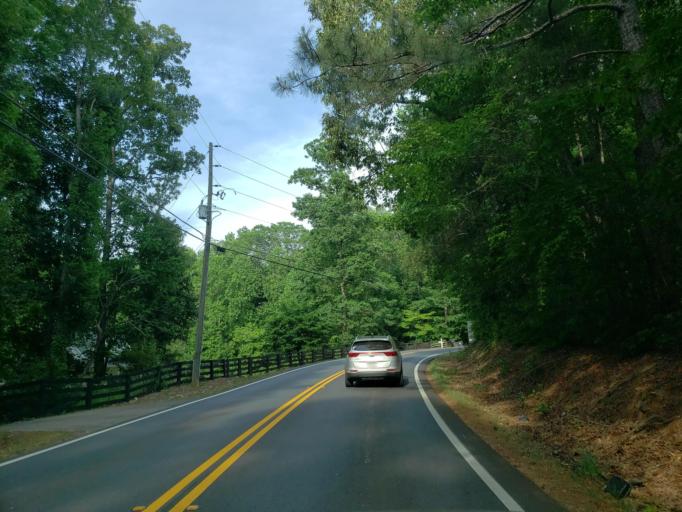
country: US
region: Georgia
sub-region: Fulton County
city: Milton
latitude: 34.1749
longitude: -84.3852
